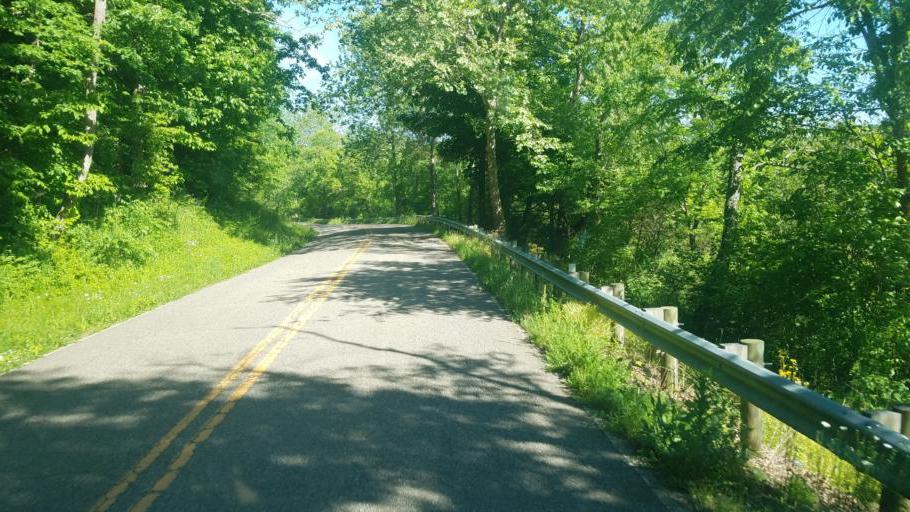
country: US
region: Ohio
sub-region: Tuscarawas County
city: Newcomerstown
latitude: 40.1830
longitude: -81.6069
